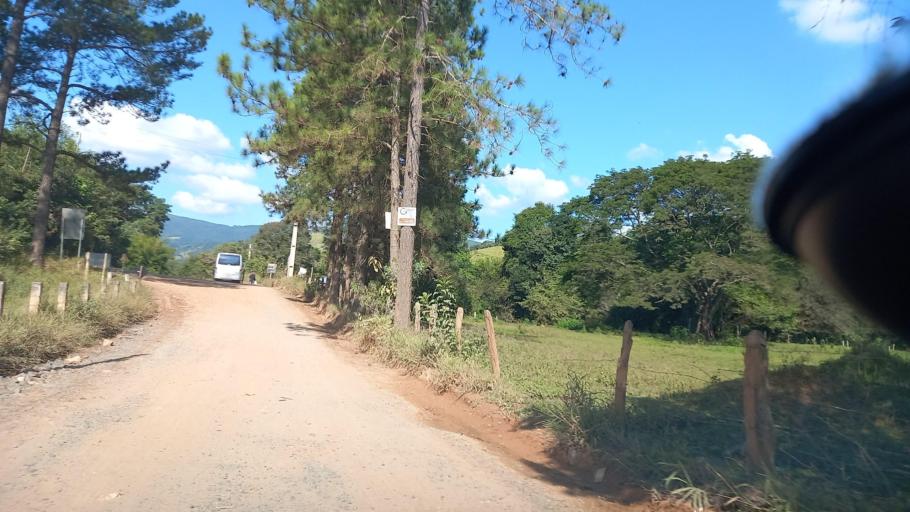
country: BR
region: Minas Gerais
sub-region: Camanducaia
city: Camanducaia
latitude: -22.7773
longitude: -46.1611
